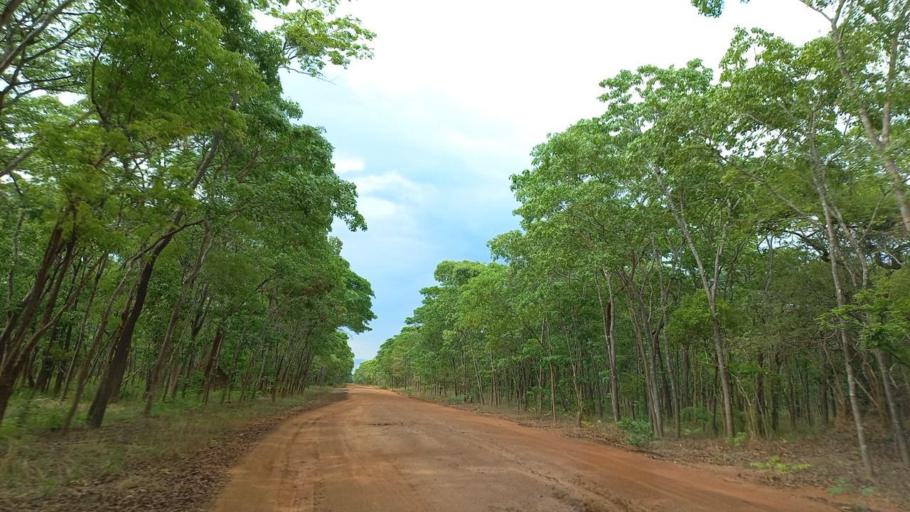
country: ZM
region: North-Western
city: Kalengwa
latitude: -13.4027
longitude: 25.0658
